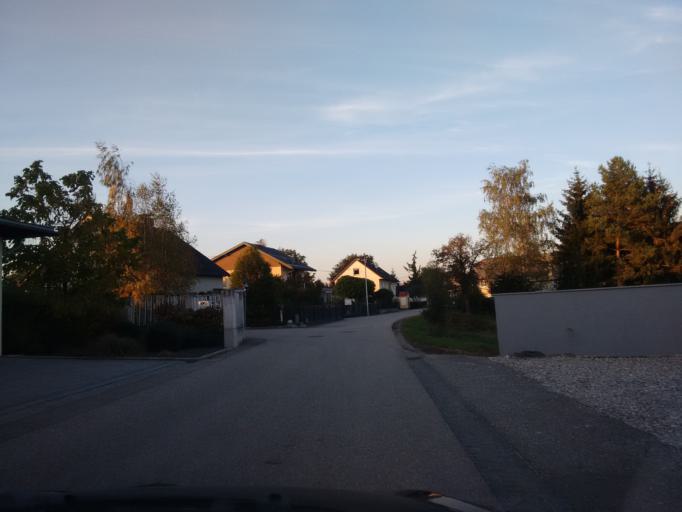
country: AT
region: Upper Austria
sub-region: Wels-Land
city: Gunskirchen
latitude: 48.1489
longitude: 13.9643
